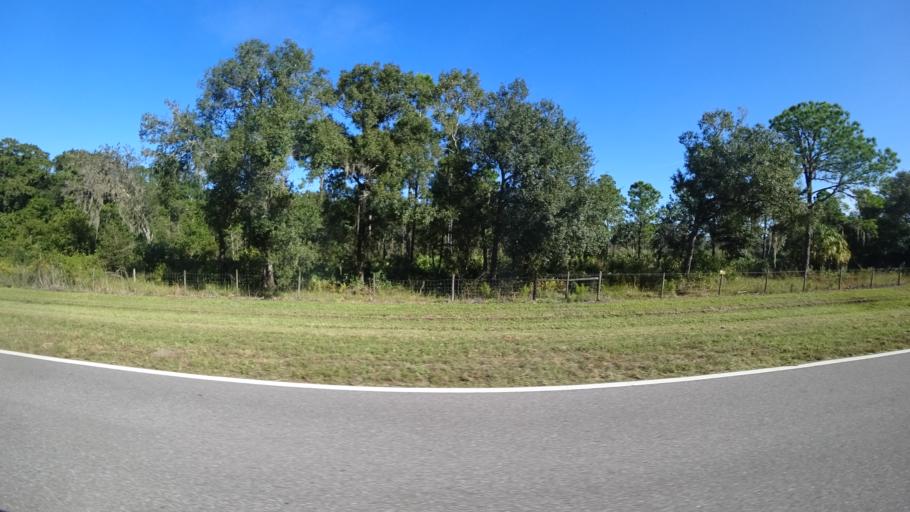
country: US
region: Florida
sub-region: Hillsborough County
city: Sun City Center
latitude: 27.6575
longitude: -82.3766
